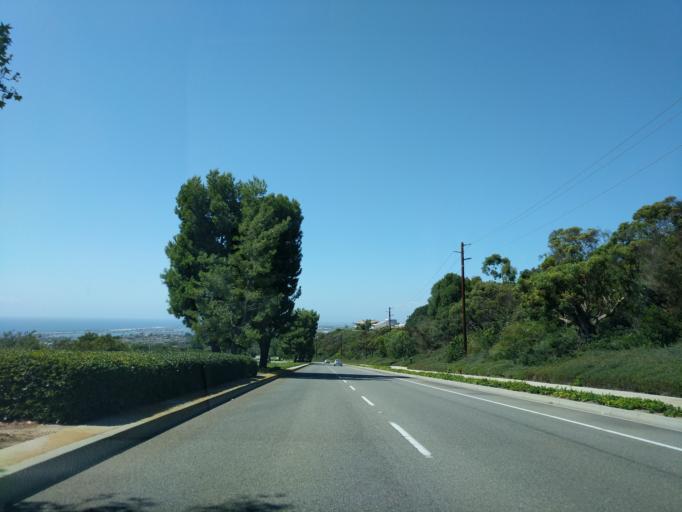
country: US
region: California
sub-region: Orange County
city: San Joaquin Hills
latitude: 33.6070
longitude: -117.8457
